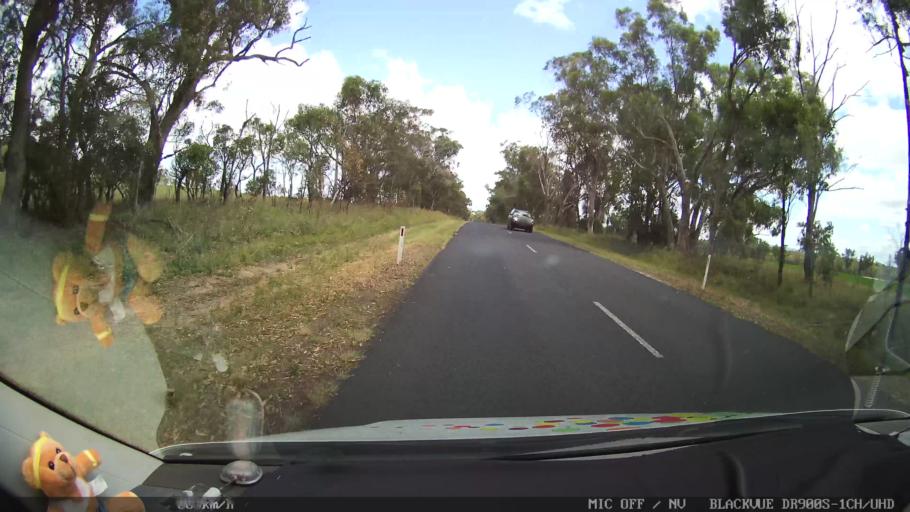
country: AU
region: New South Wales
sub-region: Glen Innes Severn
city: Glen Innes
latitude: -29.4795
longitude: 151.6828
